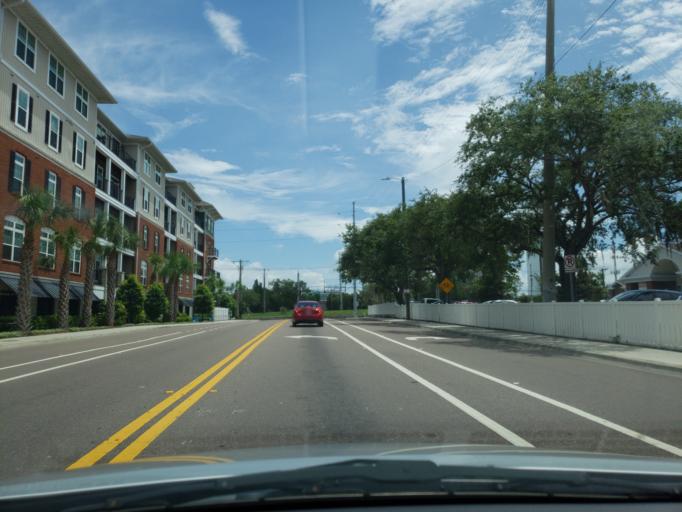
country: US
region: Florida
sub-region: Hillsborough County
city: University
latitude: 28.0701
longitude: -82.4140
